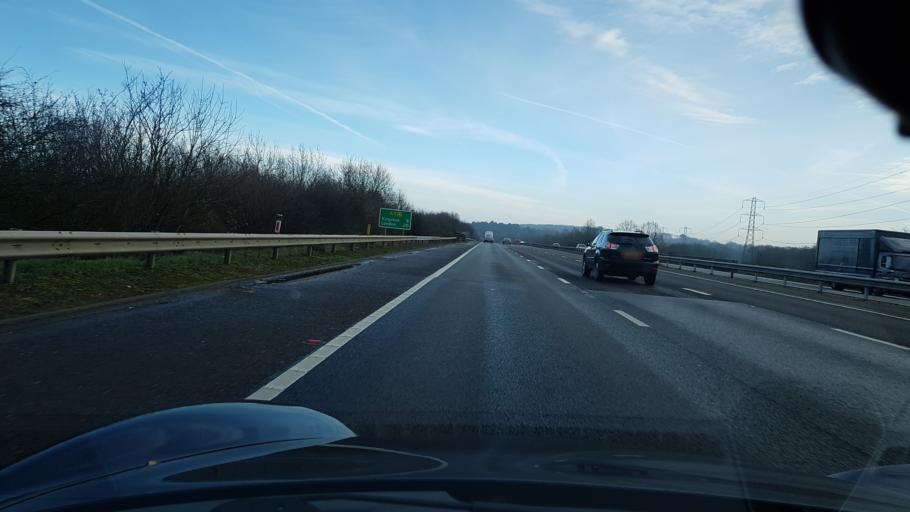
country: GB
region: England
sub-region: Surrey
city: Esher
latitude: 51.3495
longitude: -0.3516
